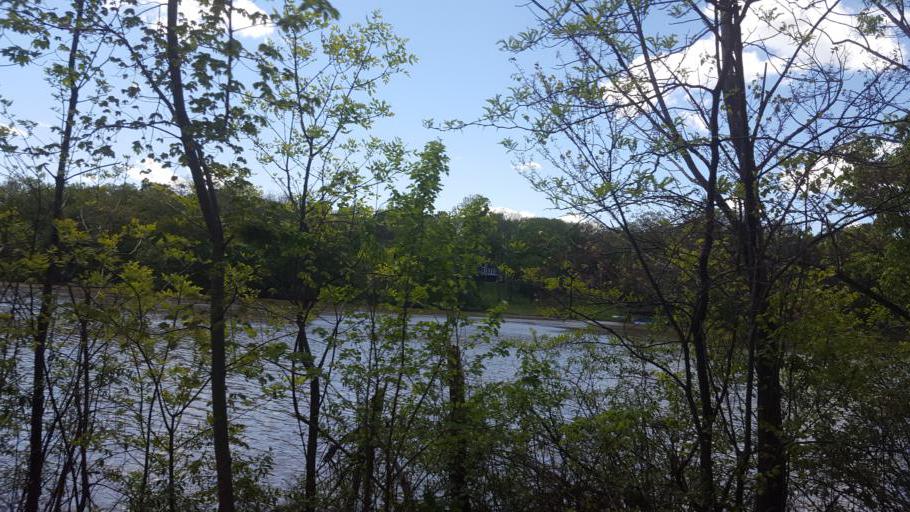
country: US
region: Ohio
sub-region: Franklin County
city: Upper Arlington
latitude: 40.0417
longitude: -83.0950
